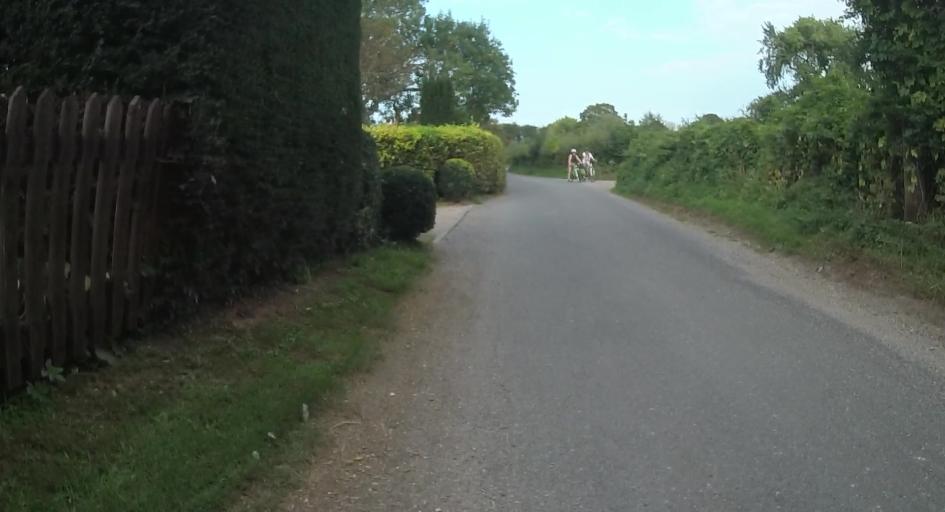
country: GB
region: England
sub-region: Hampshire
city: Kings Worthy
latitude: 51.0713
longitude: -1.1853
